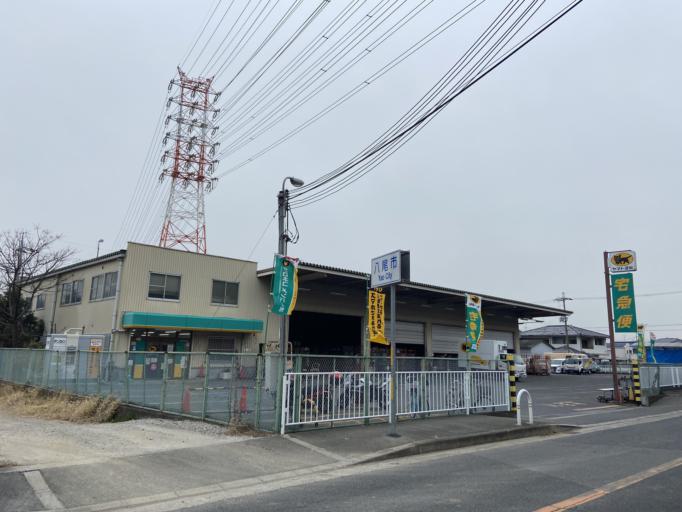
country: JP
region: Osaka
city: Kashihara
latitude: 34.6009
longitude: 135.6316
